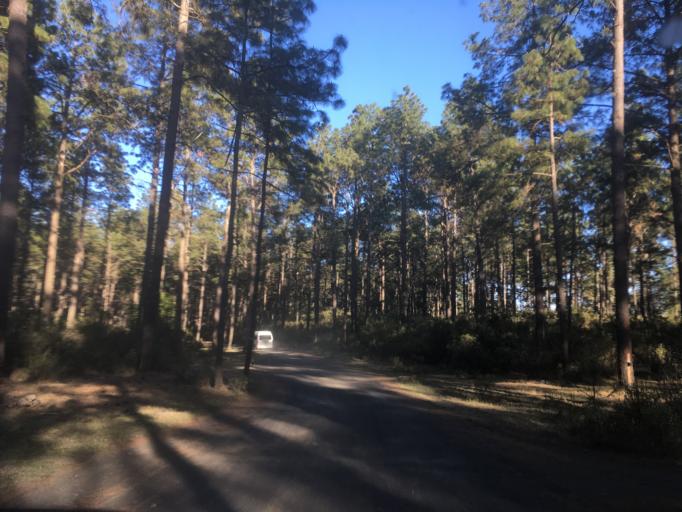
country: MX
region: Michoacan
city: Angahuan
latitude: 19.4638
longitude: -102.2313
